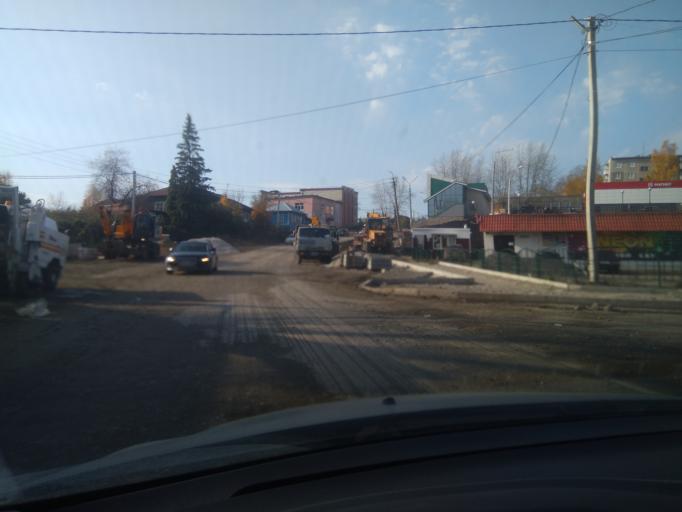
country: RU
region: Sverdlovsk
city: Nizhniye Sergi
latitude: 56.6635
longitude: 59.3051
